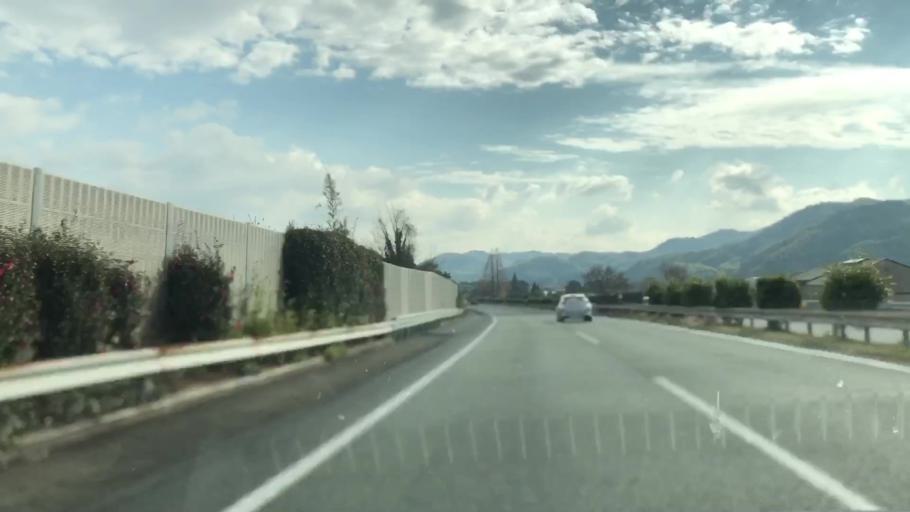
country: JP
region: Fukuoka
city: Setakamachi-takayanagi
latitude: 33.1250
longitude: 130.5186
